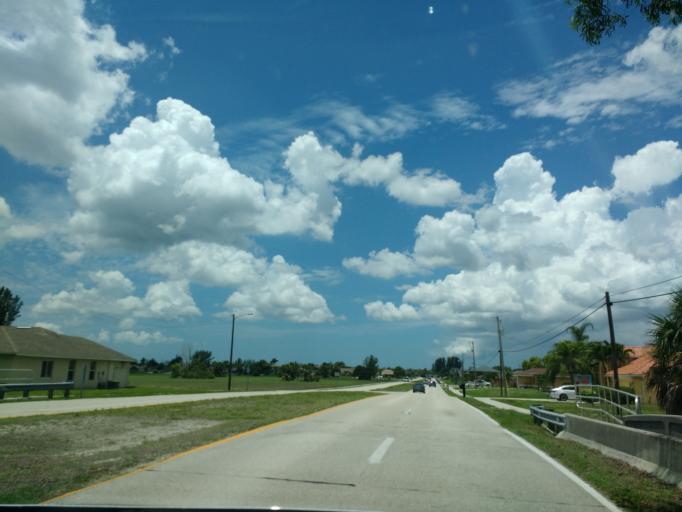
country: US
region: Florida
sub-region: Lee County
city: Cape Coral
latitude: 26.5838
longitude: -82.0095
